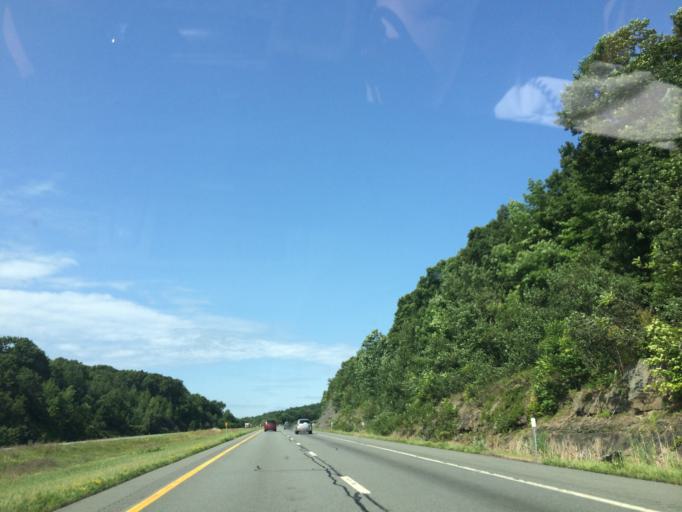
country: US
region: New York
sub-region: Orange County
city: Otisville
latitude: 41.3992
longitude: -74.5236
